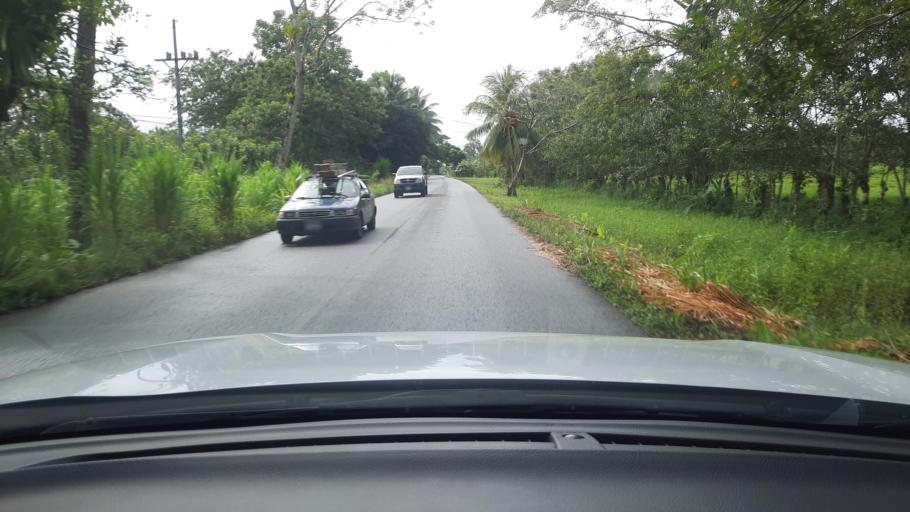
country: CR
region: Alajuela
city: Upala
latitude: 10.9239
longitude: -85.0685
